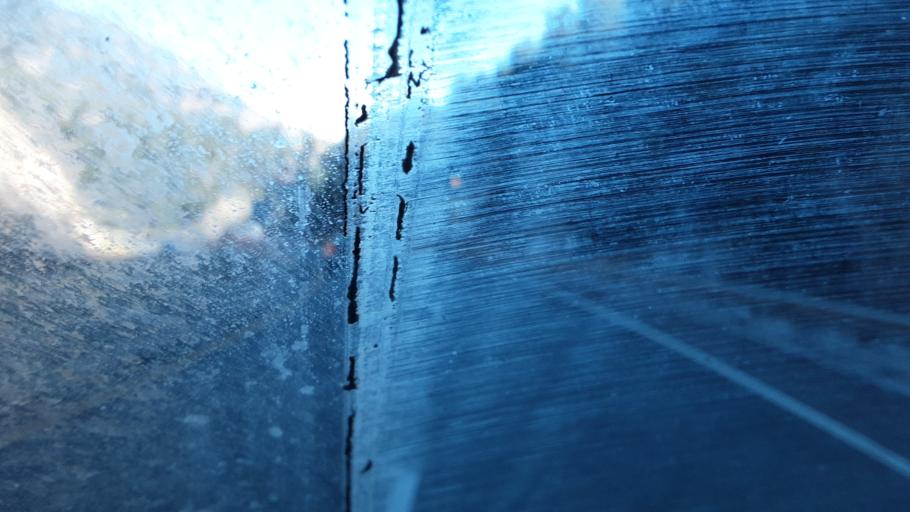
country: US
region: Colorado
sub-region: Jefferson County
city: Indian Hills
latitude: 39.6179
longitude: -105.2241
